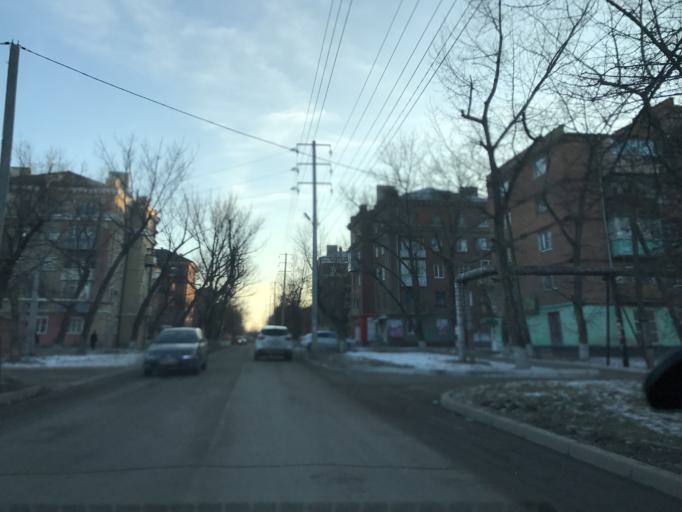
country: RU
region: Rostov
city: Kamensk-Shakhtinskiy
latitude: 48.3191
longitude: 40.2641
